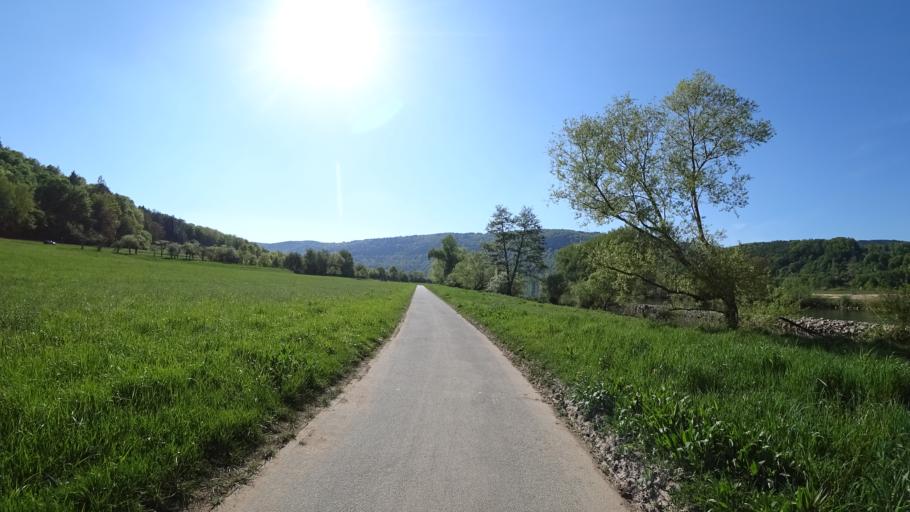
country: DE
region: Baden-Wuerttemberg
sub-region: Regierungsbezirk Stuttgart
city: Freudenberg
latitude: 49.7400
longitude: 9.2986
